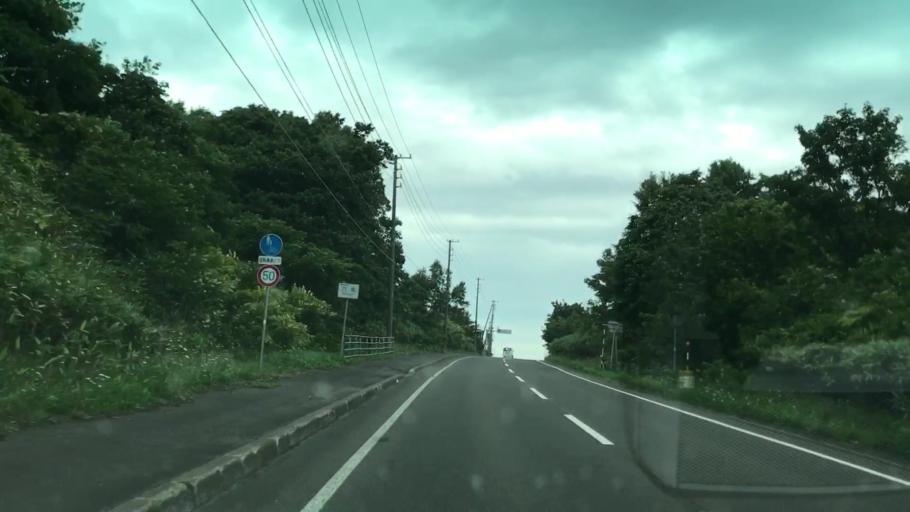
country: JP
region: Hokkaido
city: Iwanai
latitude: 42.7778
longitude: 140.2385
